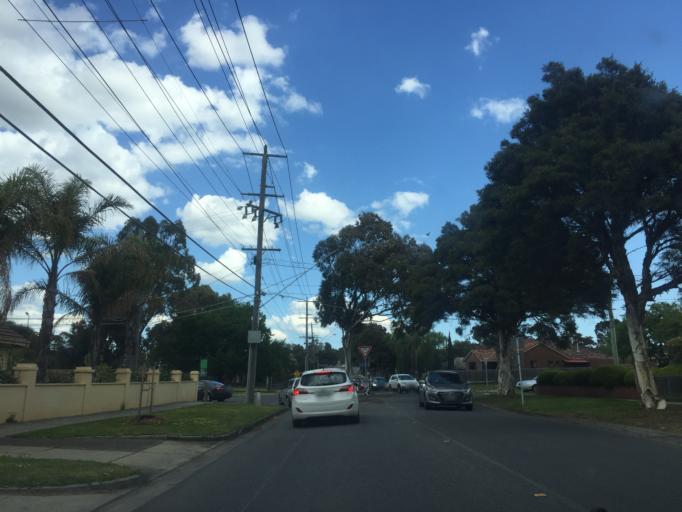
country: AU
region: Victoria
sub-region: Darebin
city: Kingsbury
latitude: -37.7146
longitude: 145.0222
